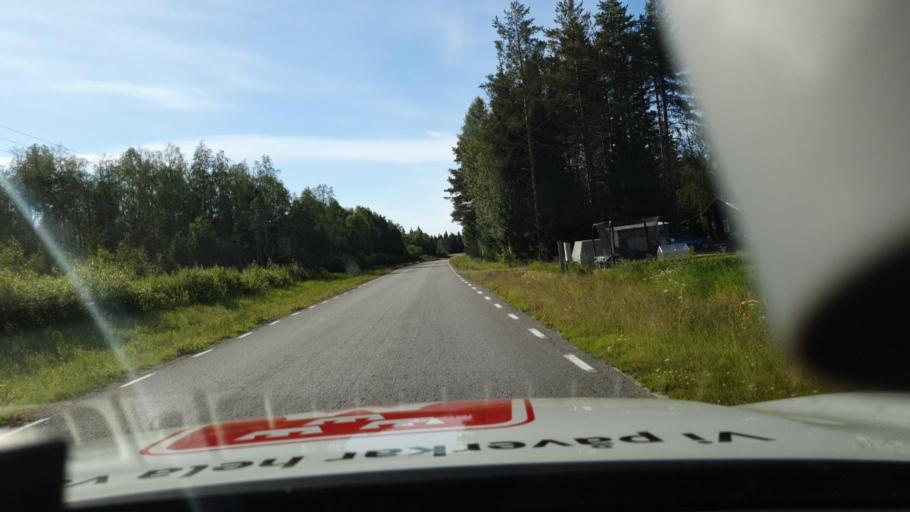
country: SE
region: Norrbotten
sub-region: Kalix Kommun
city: Toere
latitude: 65.8923
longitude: 22.6398
